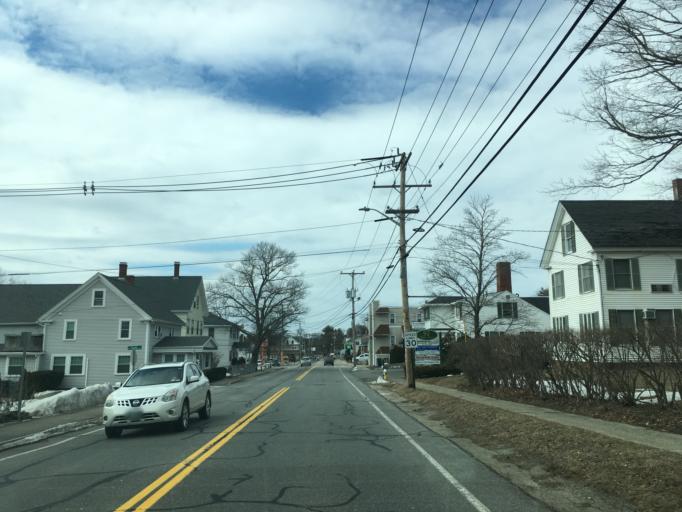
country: US
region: New Hampshire
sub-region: Rockingham County
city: Hampton
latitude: 42.9408
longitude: -70.8345
